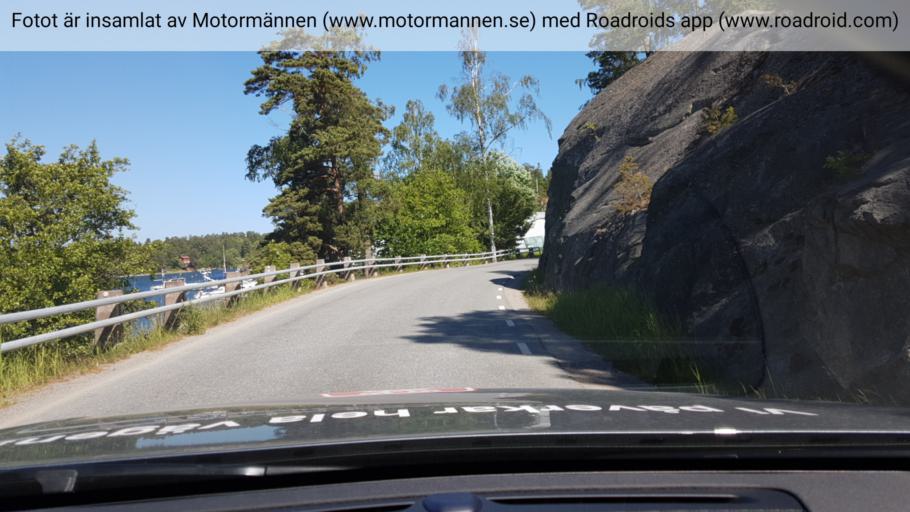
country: SE
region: Stockholm
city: Dalaro
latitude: 59.1513
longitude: 18.4334
